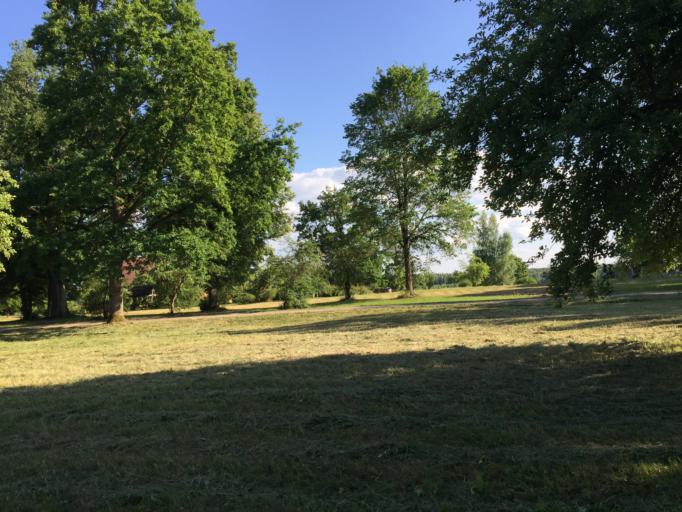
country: LV
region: Aizkraukles Rajons
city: Aizkraukle
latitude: 56.7909
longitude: 25.2673
